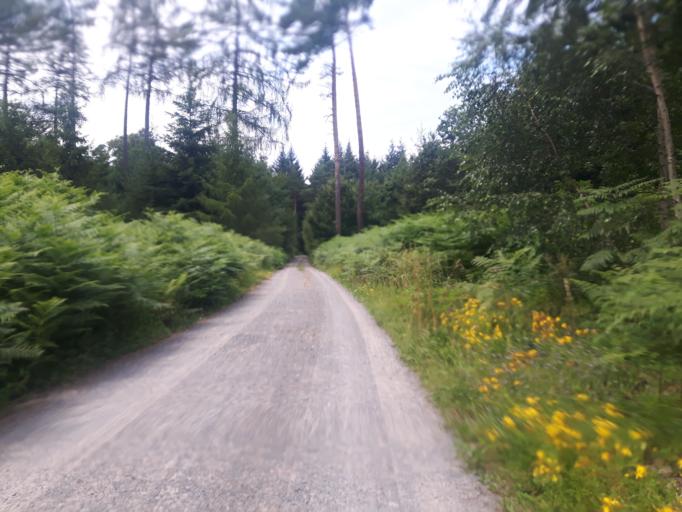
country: DE
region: Baden-Wuerttemberg
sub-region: Regierungsbezirk Stuttgart
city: Cleebronn
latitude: 49.0302
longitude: 9.0235
